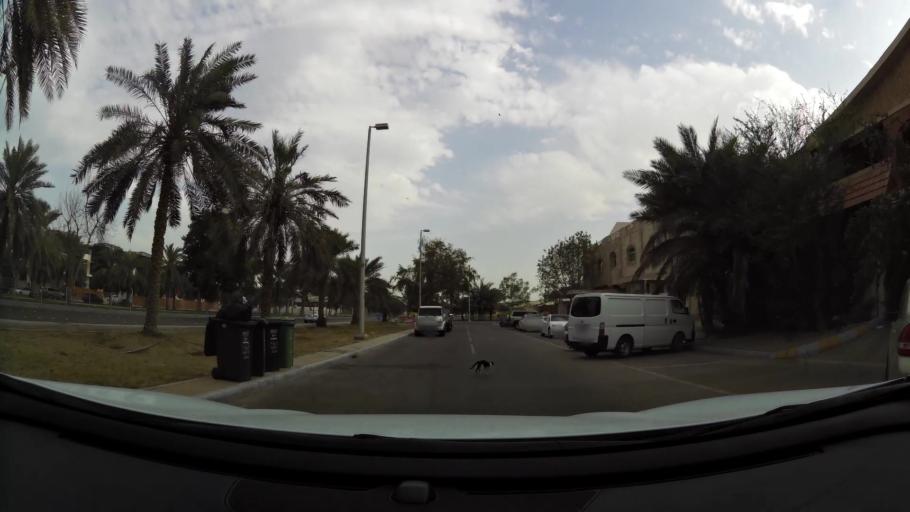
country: AE
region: Abu Dhabi
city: Abu Dhabi
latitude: 24.4612
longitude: 54.3559
